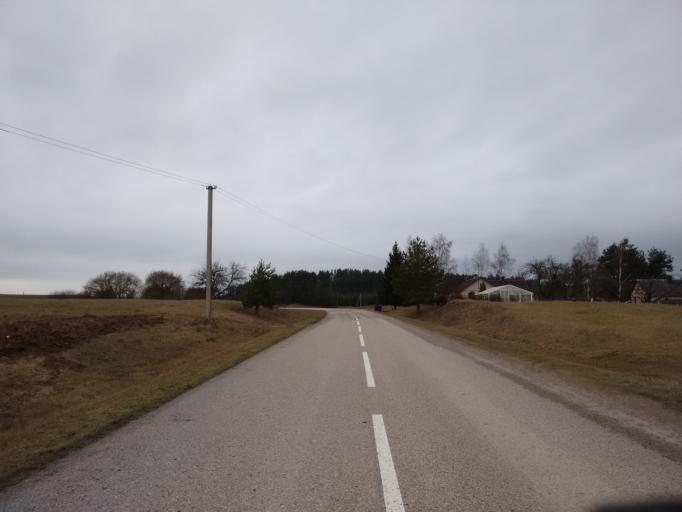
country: LT
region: Alytaus apskritis
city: Druskininkai
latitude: 54.2213
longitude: 23.9048
